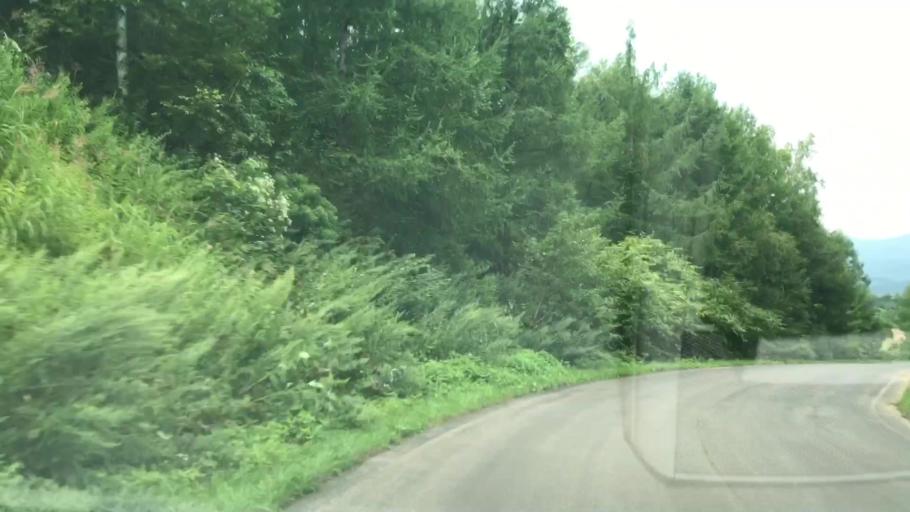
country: JP
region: Hokkaido
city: Yoichi
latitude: 43.1724
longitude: 140.8375
